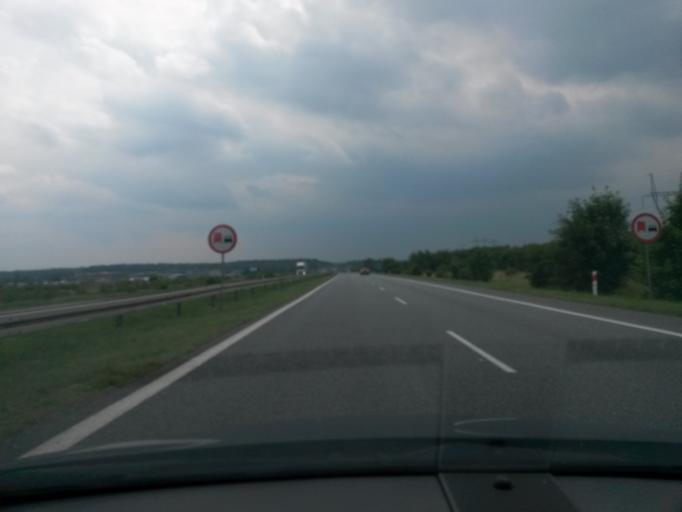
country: PL
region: Lodz Voivodeship
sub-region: Powiat radomszczanski
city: Radomsko
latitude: 51.0872
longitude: 19.3749
